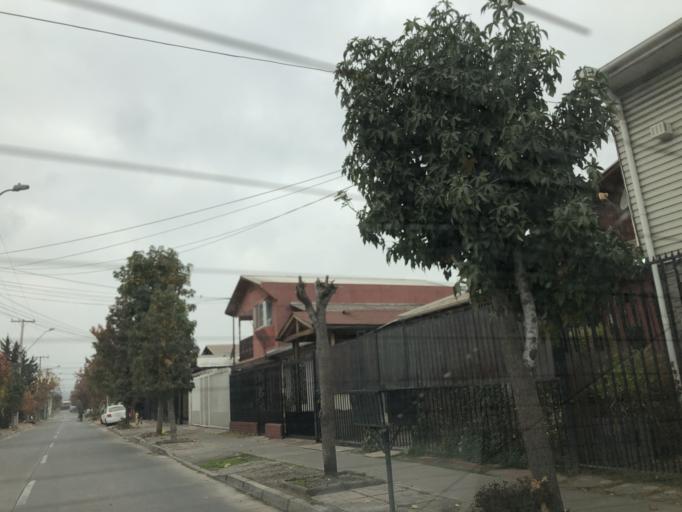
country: CL
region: Santiago Metropolitan
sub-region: Provincia de Santiago
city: La Pintana
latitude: -33.5795
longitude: -70.6076
